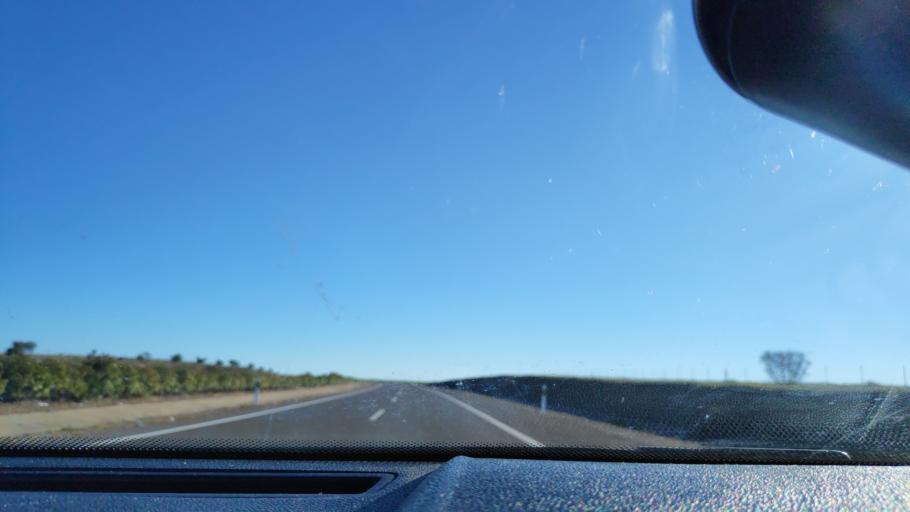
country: ES
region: Extremadura
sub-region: Provincia de Badajoz
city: Fuente de Cantos
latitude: 38.2018
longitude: -6.2856
